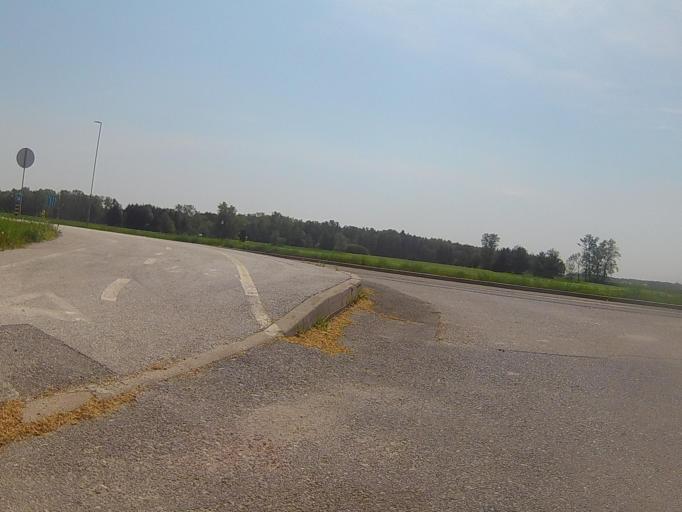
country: SI
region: Miklavz na Dravskem Polju
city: Miklavz na Dravskem Polju
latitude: 46.4968
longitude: 15.7129
